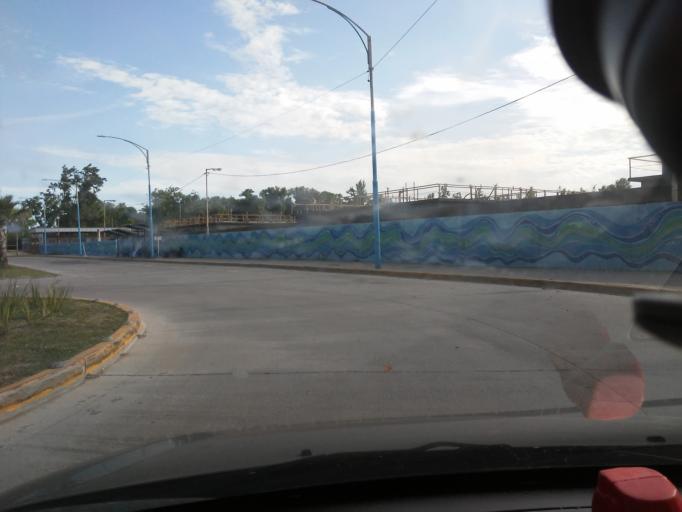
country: AR
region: Buenos Aires
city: Belen de Escobar
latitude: -34.2476
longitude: -58.7311
